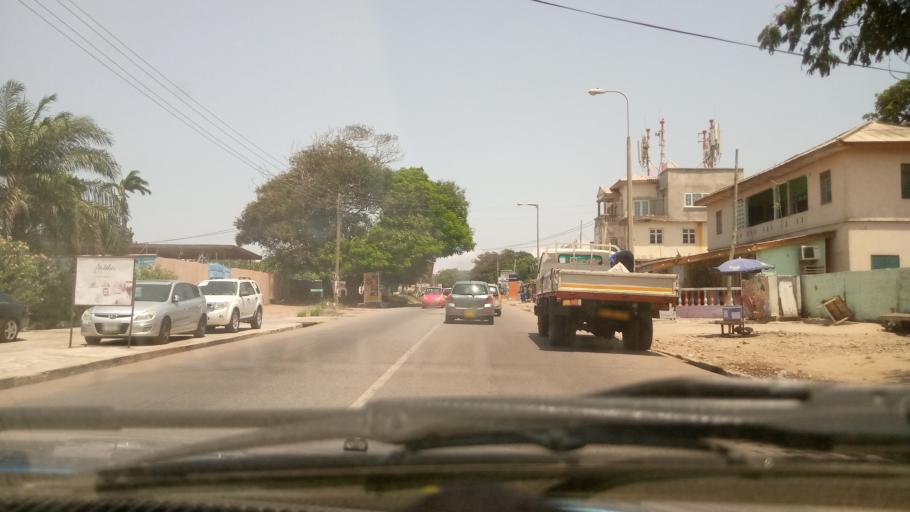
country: GH
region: Greater Accra
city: Accra
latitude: 5.5395
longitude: -0.2389
